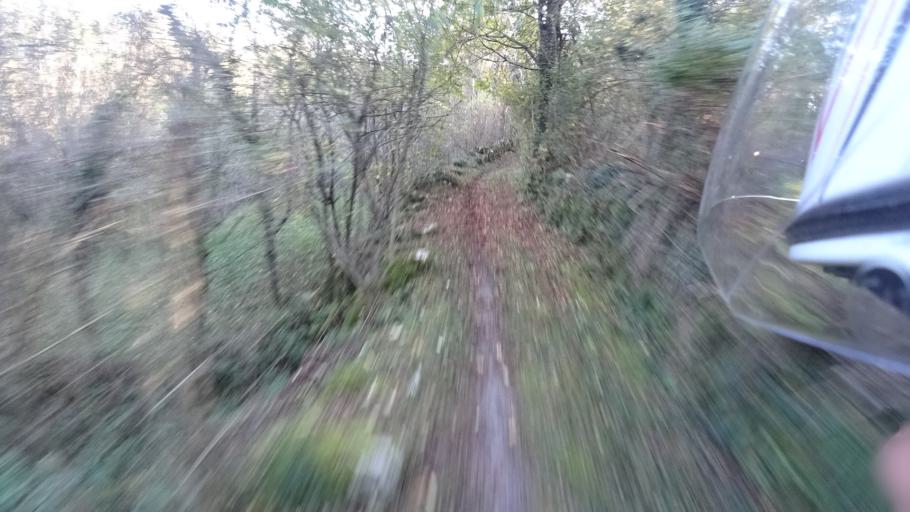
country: HR
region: Primorsko-Goranska
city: Matulji
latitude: 45.4059
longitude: 14.2856
